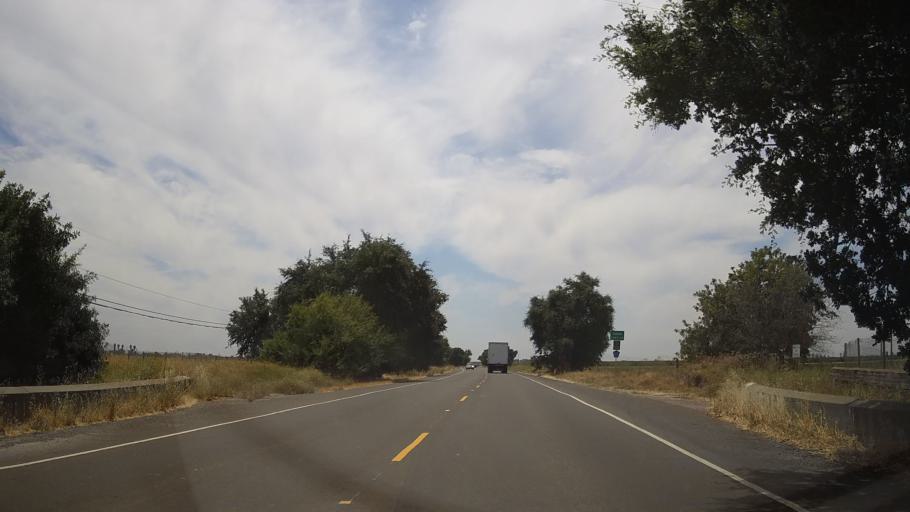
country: US
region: California
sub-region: Yolo County
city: Davis
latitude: 38.5264
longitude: -121.8035
